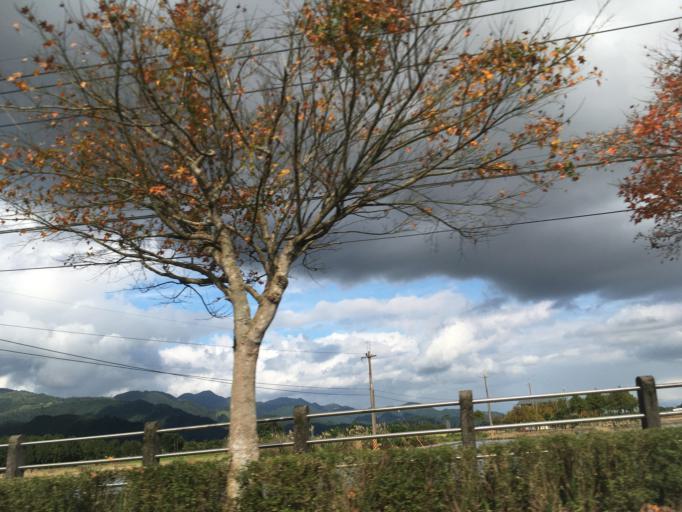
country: TW
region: Taiwan
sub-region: Yilan
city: Yilan
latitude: 24.6658
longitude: 121.6166
